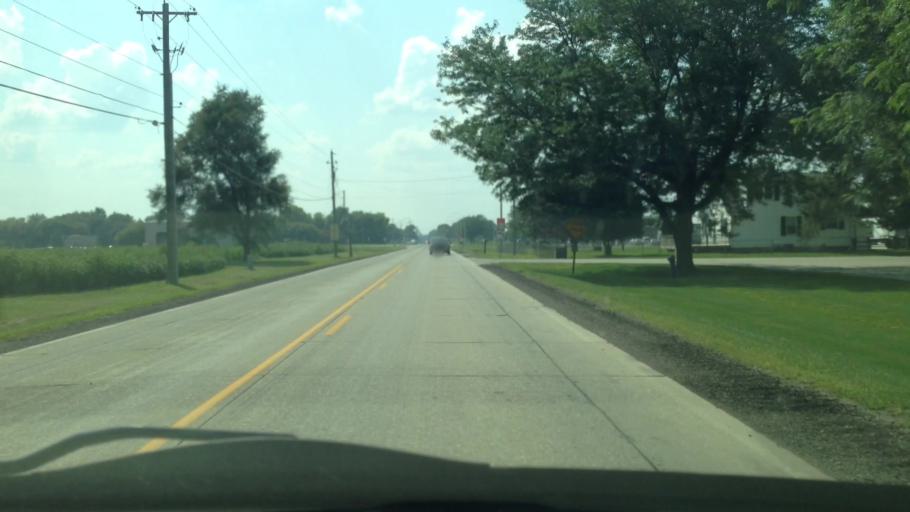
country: US
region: Iowa
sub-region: Black Hawk County
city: Cedar Falls
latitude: 42.5420
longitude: -92.3911
